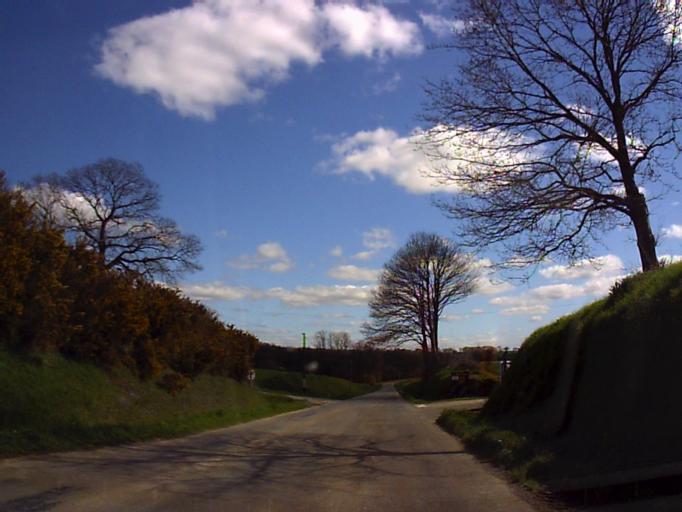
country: FR
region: Brittany
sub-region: Departement d'Ille-et-Vilaine
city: Saint-Meen-le-Grand
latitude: 48.1606
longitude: -2.1583
